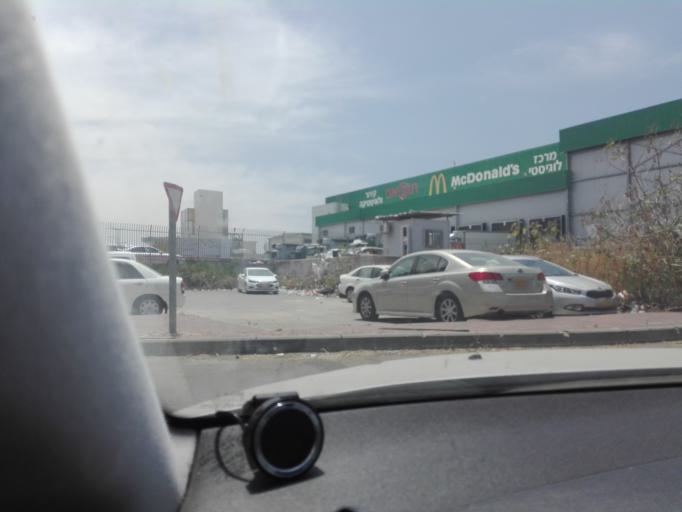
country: IL
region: Central District
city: Bene 'Ayish
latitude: 31.7246
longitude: 34.7547
